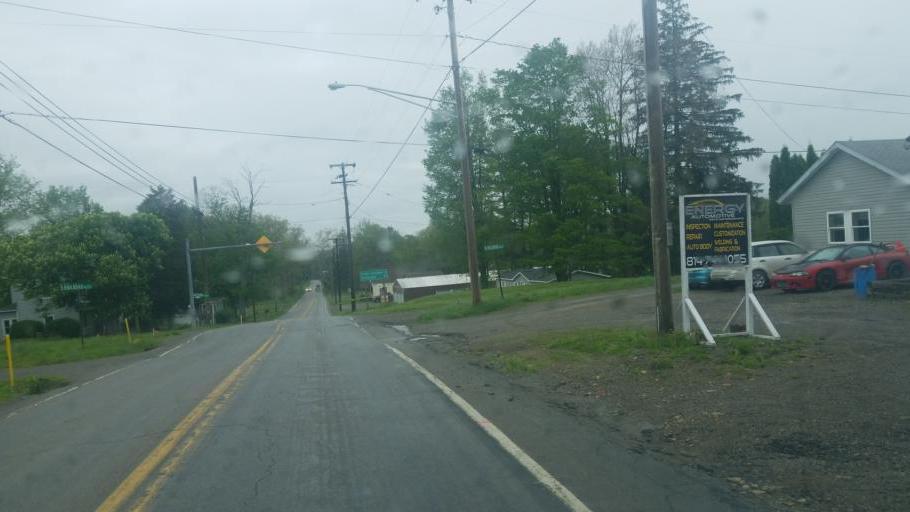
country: US
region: Pennsylvania
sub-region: Clarion County
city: Marianne
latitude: 41.3718
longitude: -79.3060
